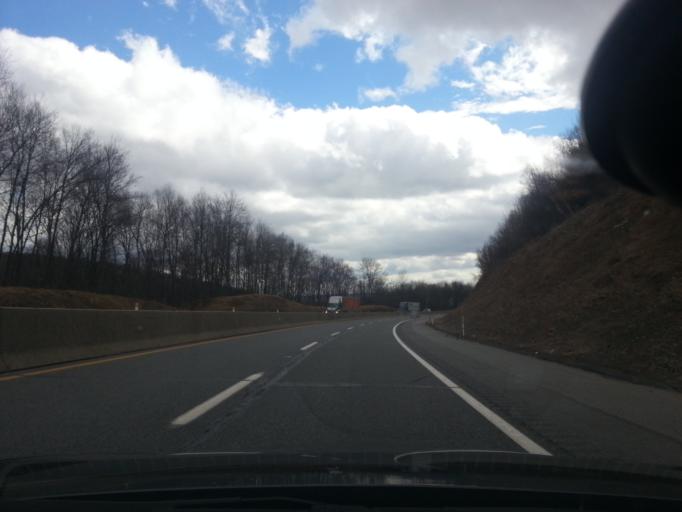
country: US
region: Pennsylvania
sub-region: Carbon County
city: Weissport East
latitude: 40.9030
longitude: -75.6394
